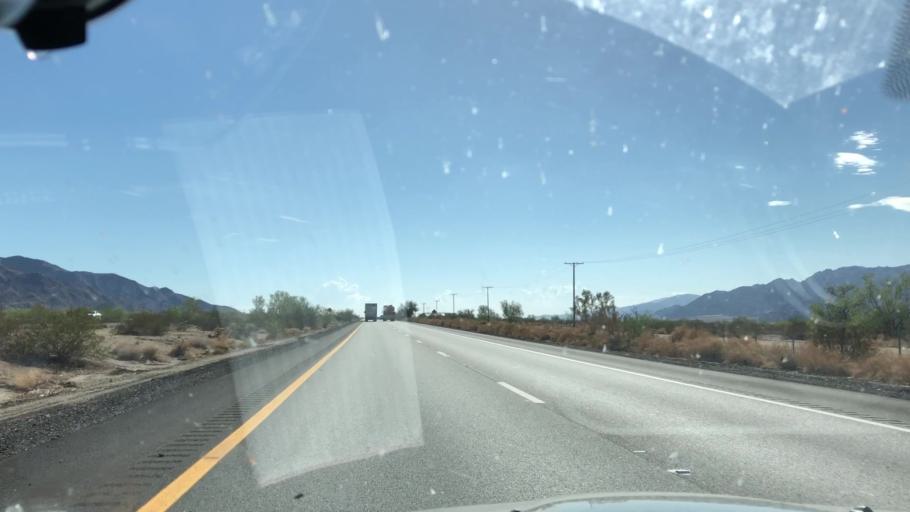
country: US
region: California
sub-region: Imperial County
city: Niland
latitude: 33.7063
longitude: -115.4340
